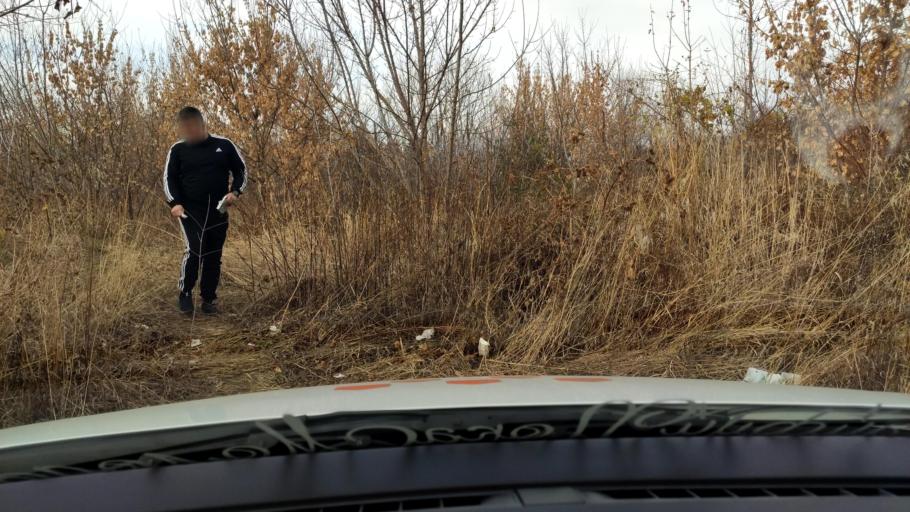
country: RU
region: Voronezj
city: Podgornoye
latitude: 51.7189
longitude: 39.1904
